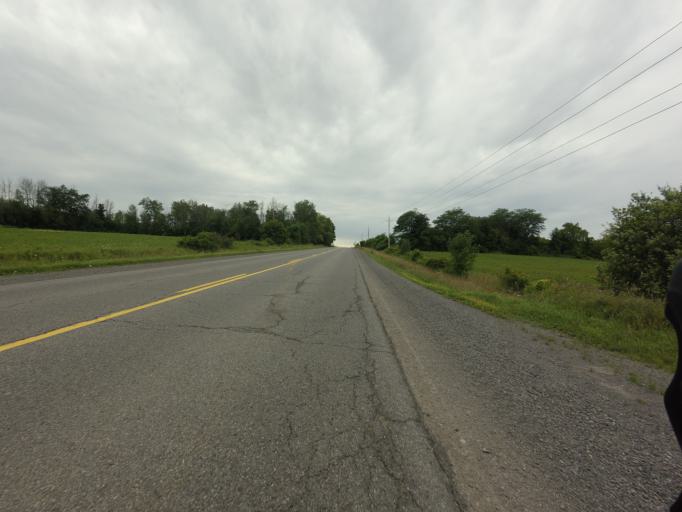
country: CA
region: Ontario
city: Ottawa
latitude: 45.2659
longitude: -75.6510
